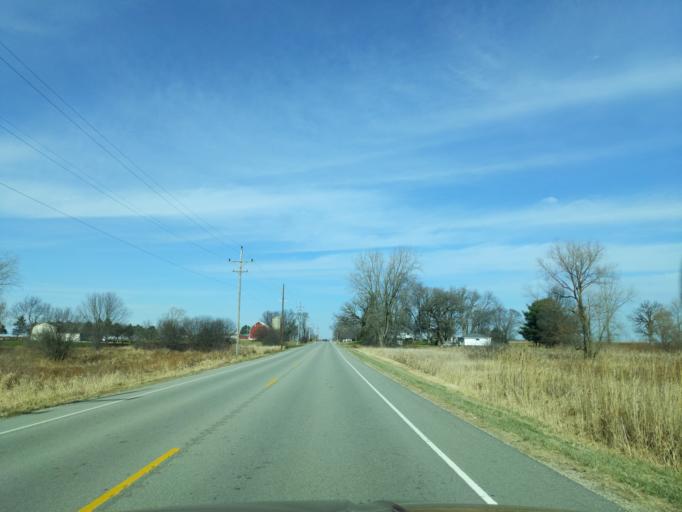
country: US
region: Wisconsin
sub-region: Walworth County
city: Elkhorn
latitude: 42.7125
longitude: -88.5817
